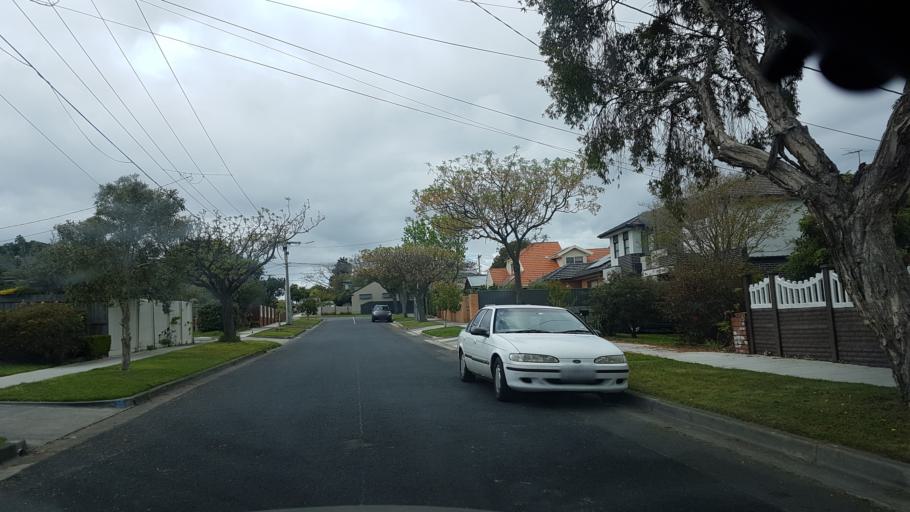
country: AU
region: Victoria
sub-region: Bayside
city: Moorabbin
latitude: -37.9294
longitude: 145.0433
